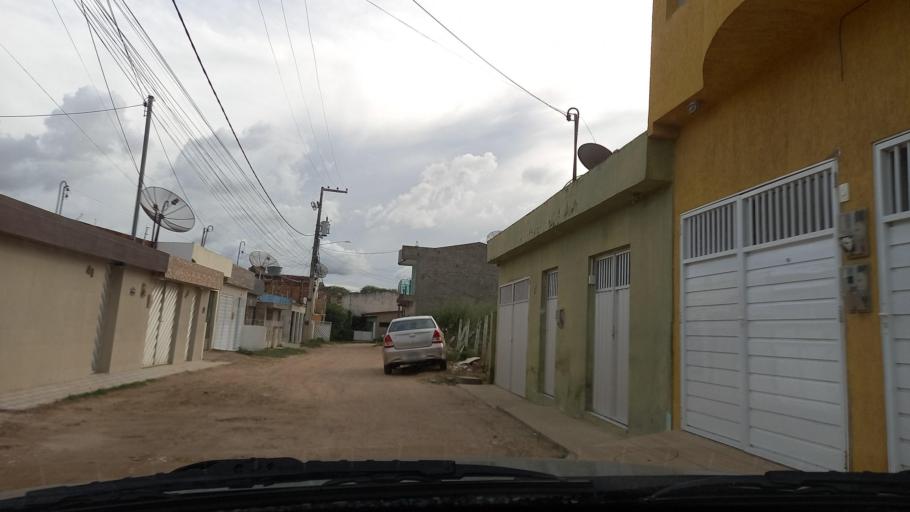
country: BR
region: Pernambuco
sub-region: Gravata
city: Gravata
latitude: -8.2014
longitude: -35.5589
